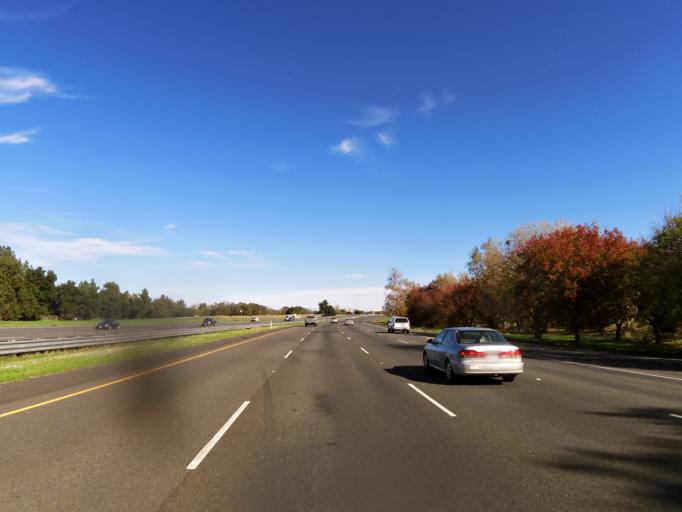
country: US
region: California
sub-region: Yolo County
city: Davis
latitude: 38.5254
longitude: -121.7638
